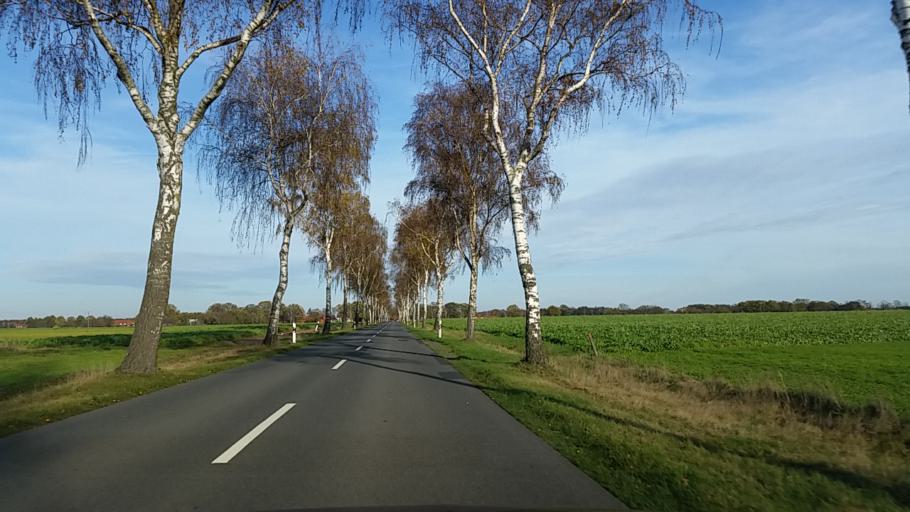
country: DE
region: Lower Saxony
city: Dedelstorf
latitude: 52.6722
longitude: 10.5162
